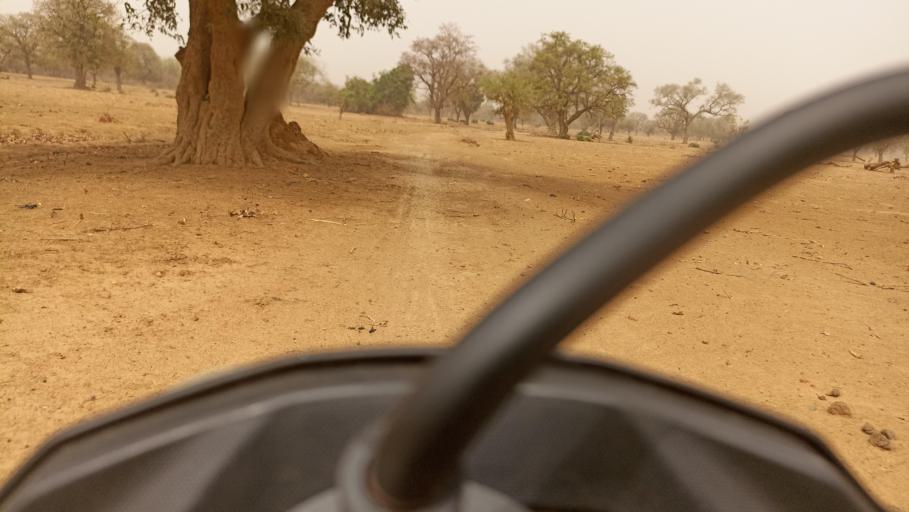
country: BF
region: Nord
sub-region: Province du Zondoma
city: Gourcy
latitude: 13.2500
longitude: -2.6033
